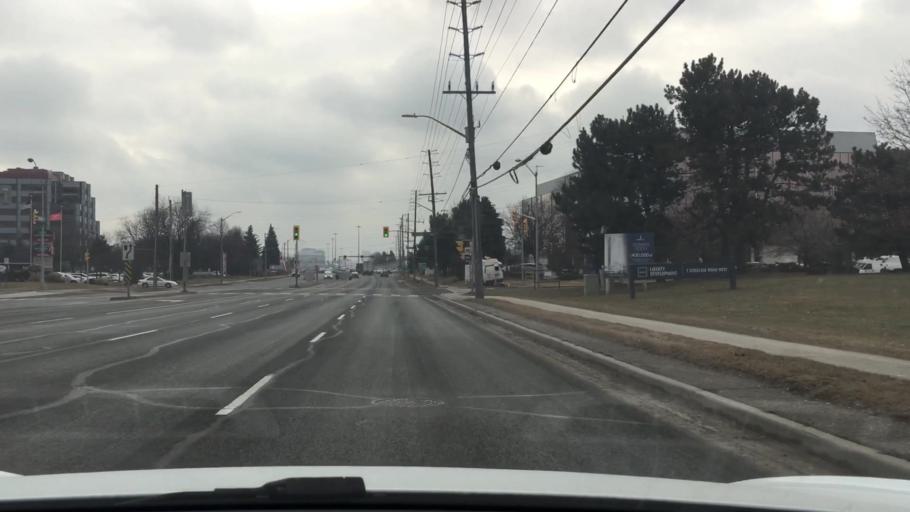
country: CA
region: Ontario
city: Willowdale
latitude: 43.8172
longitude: -79.3497
